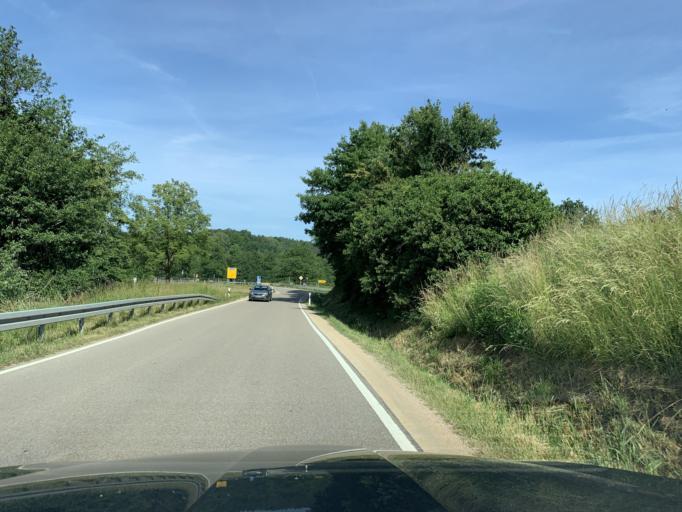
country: DE
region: Bavaria
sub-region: Upper Palatinate
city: Altendorf
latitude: 49.4002
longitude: 12.3119
